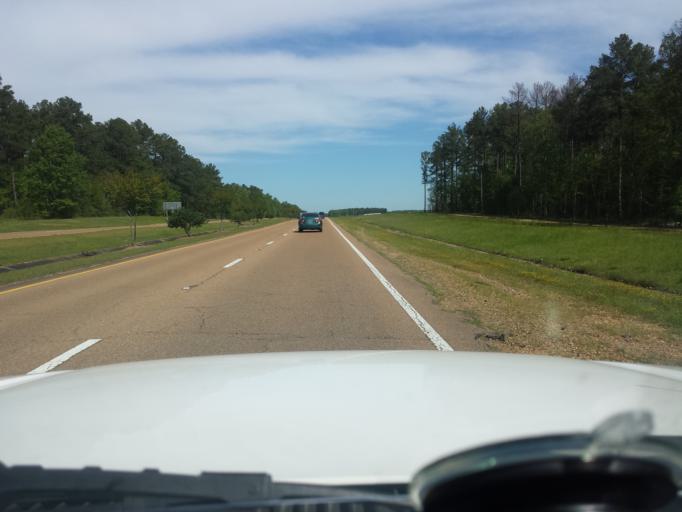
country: US
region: Mississippi
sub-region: Rankin County
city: Pearl
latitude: 32.2990
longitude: -90.0820
